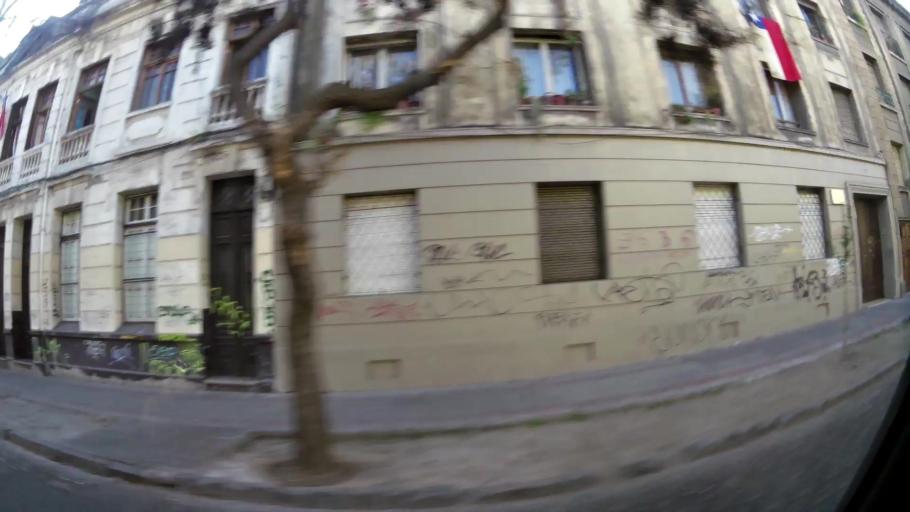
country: CL
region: Santiago Metropolitan
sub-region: Provincia de Santiago
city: Santiago
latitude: -33.4449
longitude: -70.6653
